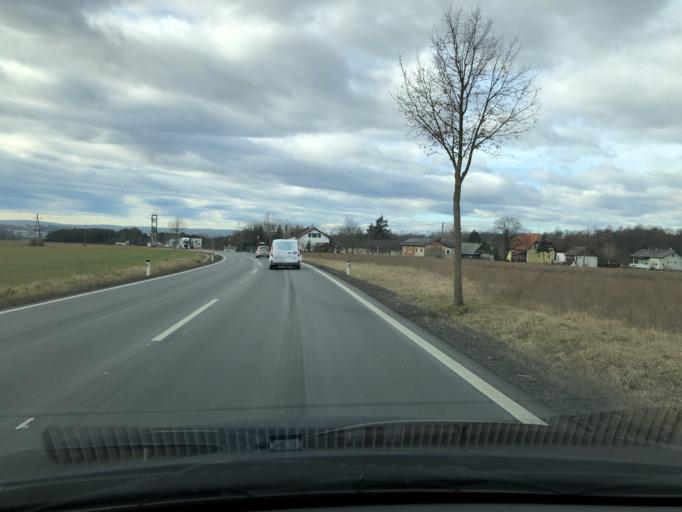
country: AT
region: Burgenland
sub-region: Politischer Bezirk Oberwart
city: Grosspetersdorf
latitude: 47.2576
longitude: 16.3520
